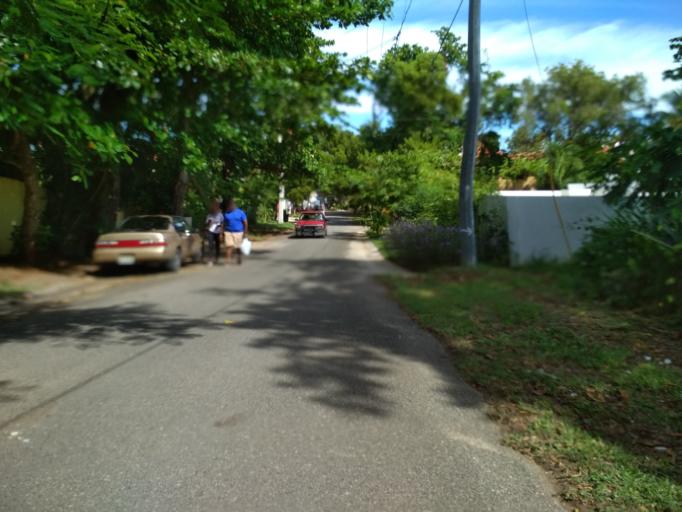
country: DO
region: Puerto Plata
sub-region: Puerto Plata
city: Puerto Plata
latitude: 19.8127
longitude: -70.7119
